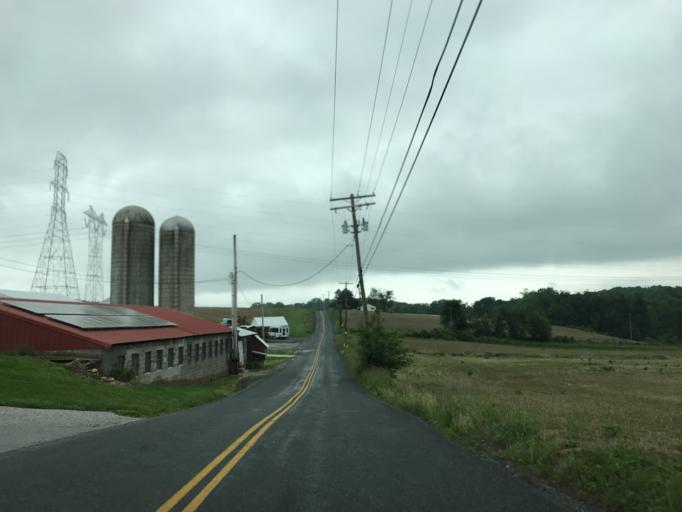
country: US
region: Maryland
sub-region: Harford County
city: Jarrettsville
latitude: 39.6930
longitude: -76.4508
